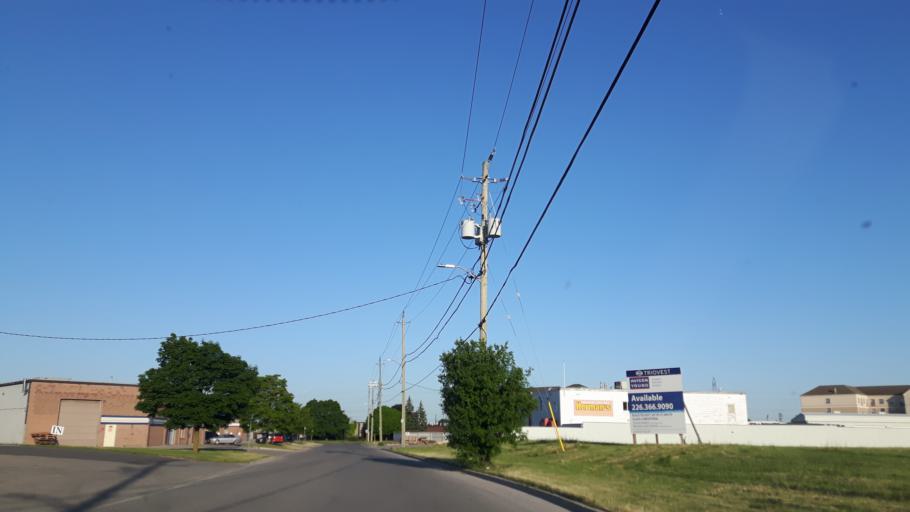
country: CA
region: Ontario
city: London
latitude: 42.9299
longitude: -81.2152
